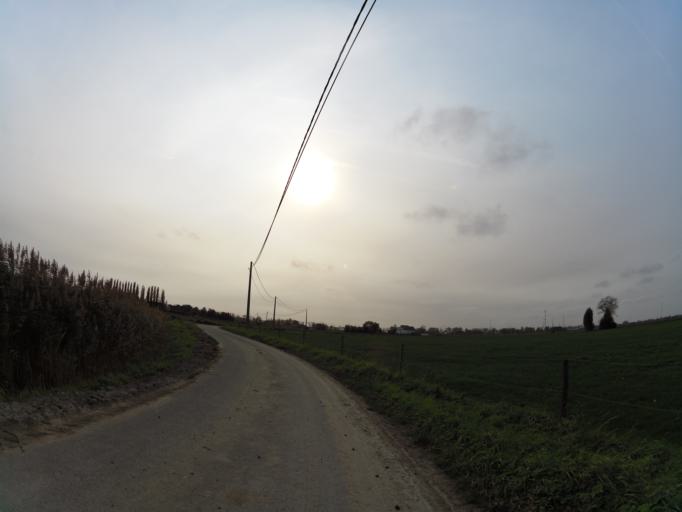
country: BE
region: Flanders
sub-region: Provincie West-Vlaanderen
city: Oudenburg
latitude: 51.2116
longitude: 3.0452
